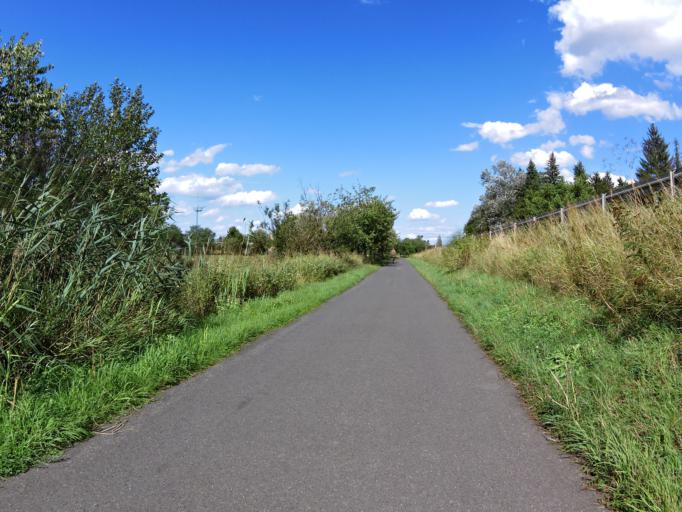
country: DE
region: Bavaria
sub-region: Regierungsbezirk Unterfranken
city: Kitzingen
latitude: 49.7182
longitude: 10.1538
